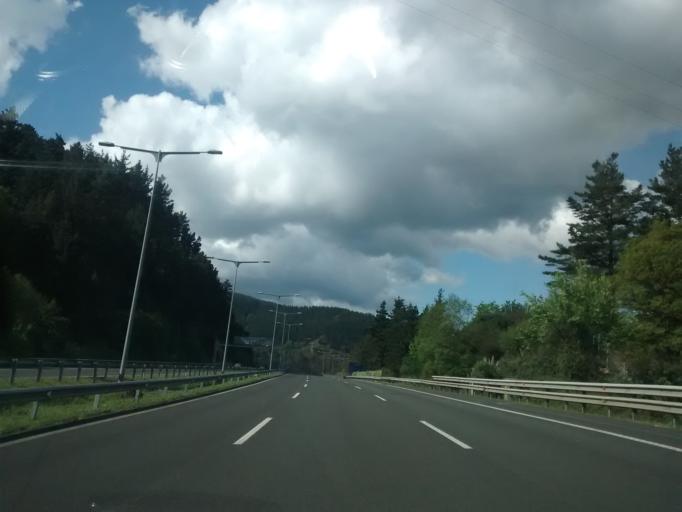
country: ES
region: Basque Country
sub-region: Bizkaia
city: Arrigorriaga
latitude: 43.1809
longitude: -2.8984
